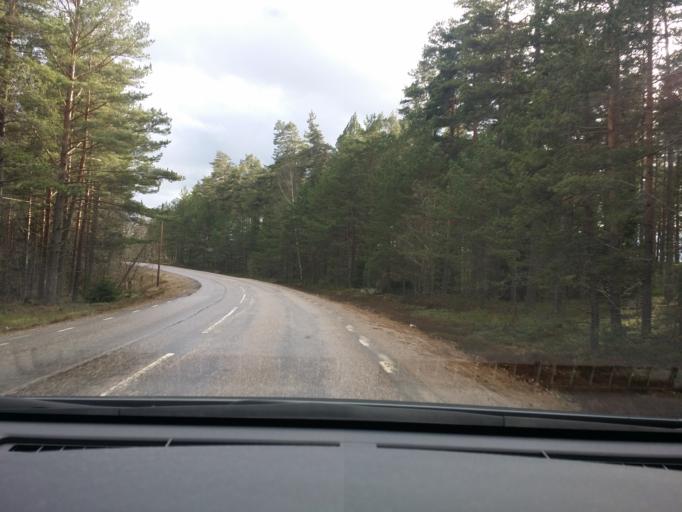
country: SE
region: Soedermanland
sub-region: Eskilstuna Kommun
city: Arla
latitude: 59.3018
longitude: 16.6783
